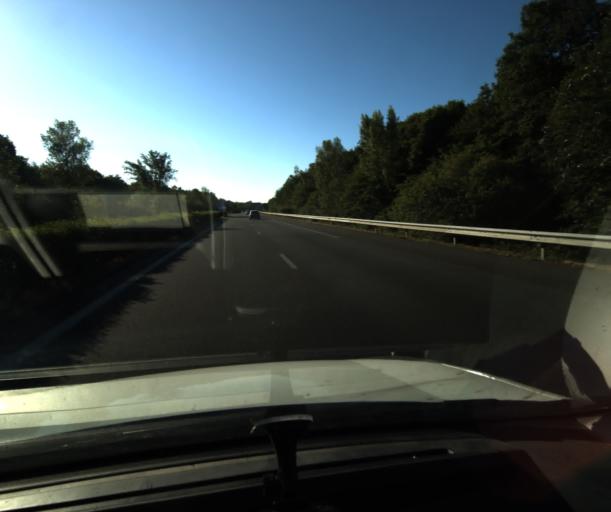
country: FR
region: Midi-Pyrenees
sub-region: Departement du Tarn-et-Garonne
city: Saint-Porquier
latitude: 44.0109
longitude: 1.2111
